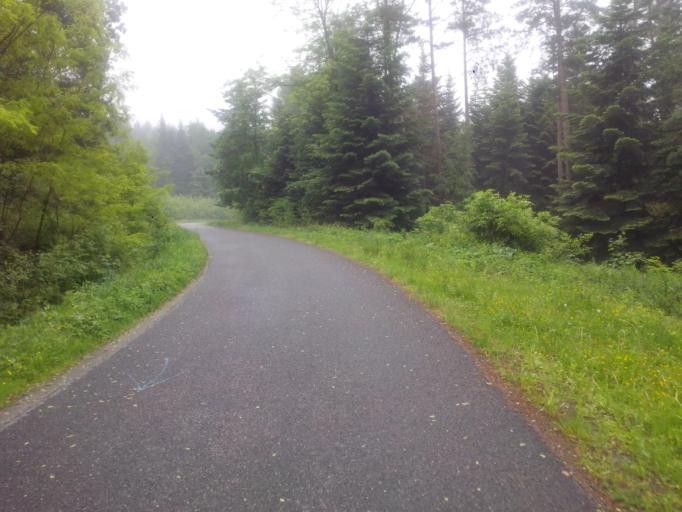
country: PL
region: Subcarpathian Voivodeship
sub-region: Powiat strzyzowski
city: Wysoka Strzyzowska
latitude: 49.8246
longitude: 21.7830
